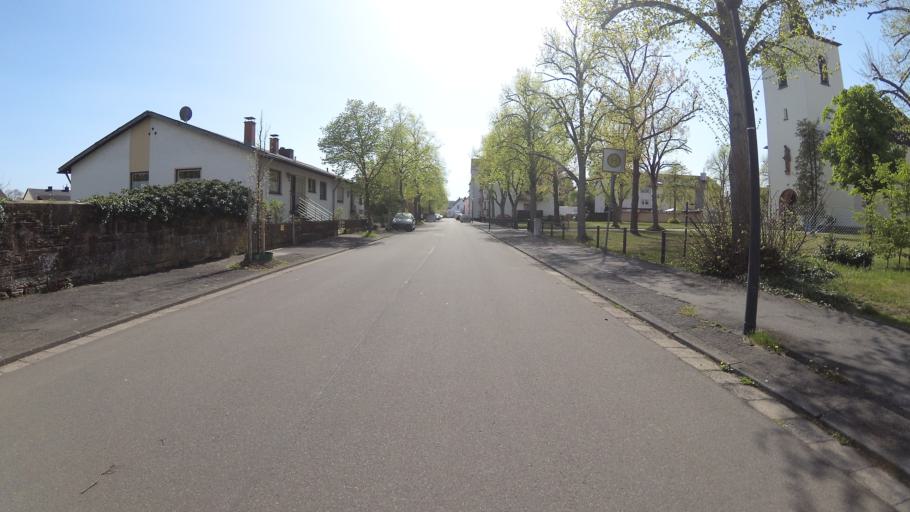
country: DE
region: Saarland
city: Homburg
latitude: 49.3108
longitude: 7.3164
